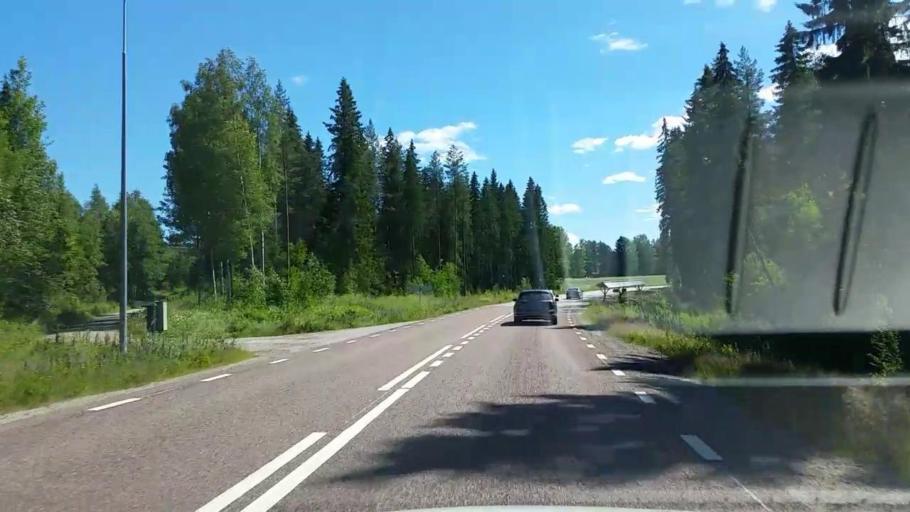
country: SE
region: Gaevleborg
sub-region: Ovanakers Kommun
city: Edsbyn
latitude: 61.2019
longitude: 15.8733
